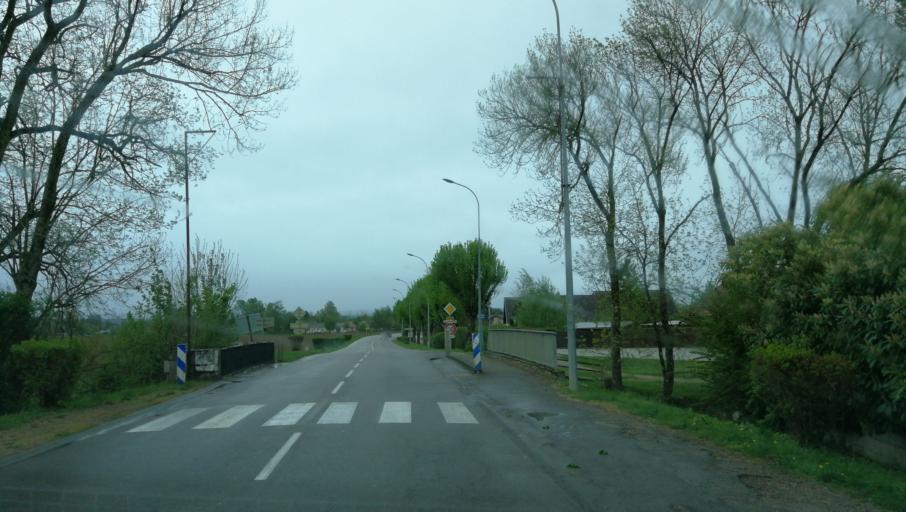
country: FR
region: Franche-Comte
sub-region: Departement du Jura
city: Bletterans
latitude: 46.7449
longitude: 5.4581
